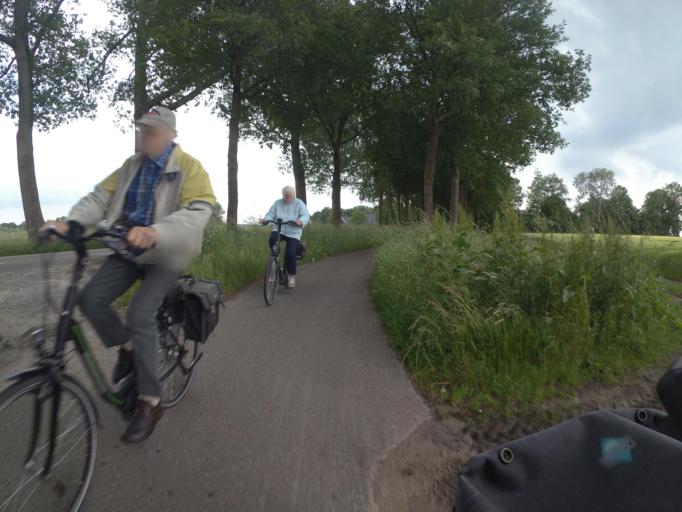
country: NL
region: Overijssel
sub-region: Gemeente Twenterand
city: Vroomshoop
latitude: 52.5268
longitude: 6.5589
